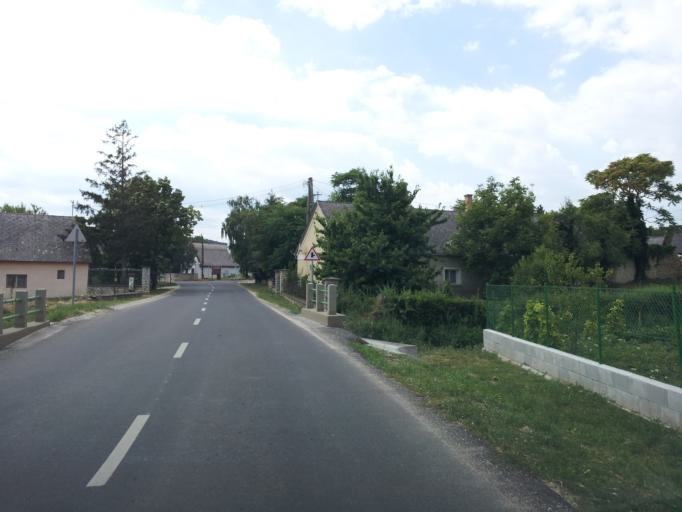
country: HU
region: Veszprem
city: Zanka
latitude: 46.9137
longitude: 17.7251
